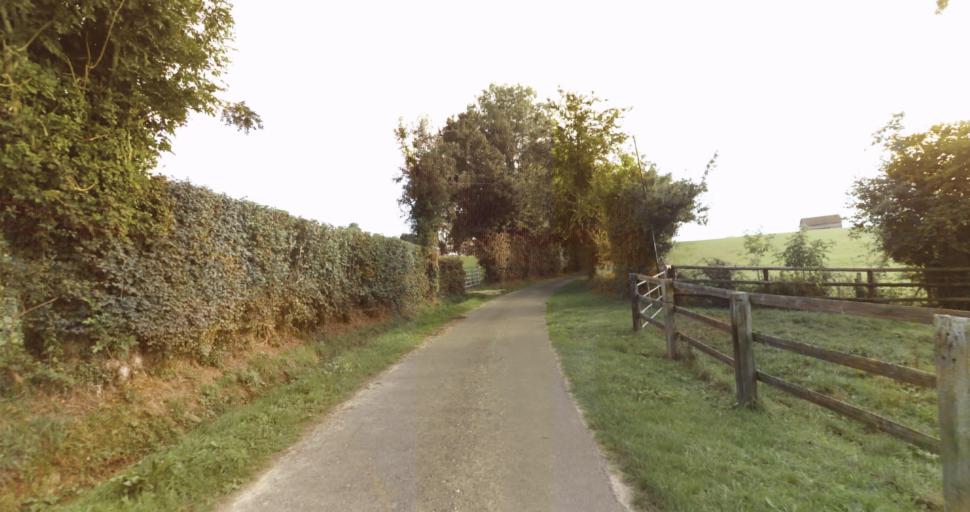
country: FR
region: Lower Normandy
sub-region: Departement de l'Orne
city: Gace
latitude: 48.7363
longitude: 0.2699
